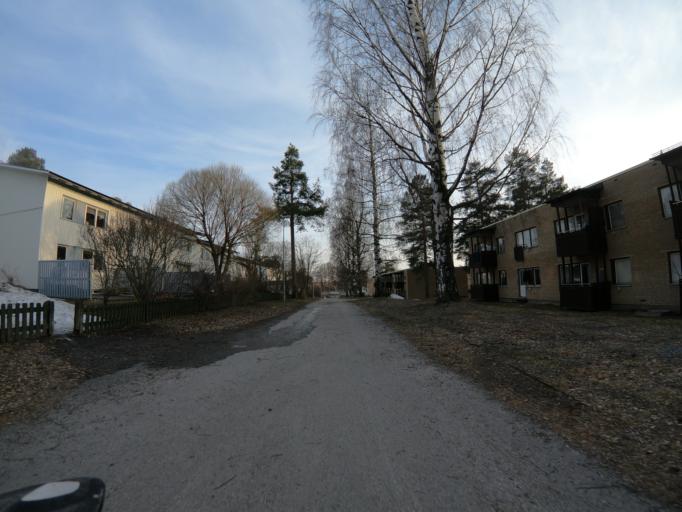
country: SE
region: Vaesterbotten
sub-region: Umea Kommun
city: Umea
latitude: 63.8406
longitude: 20.2790
